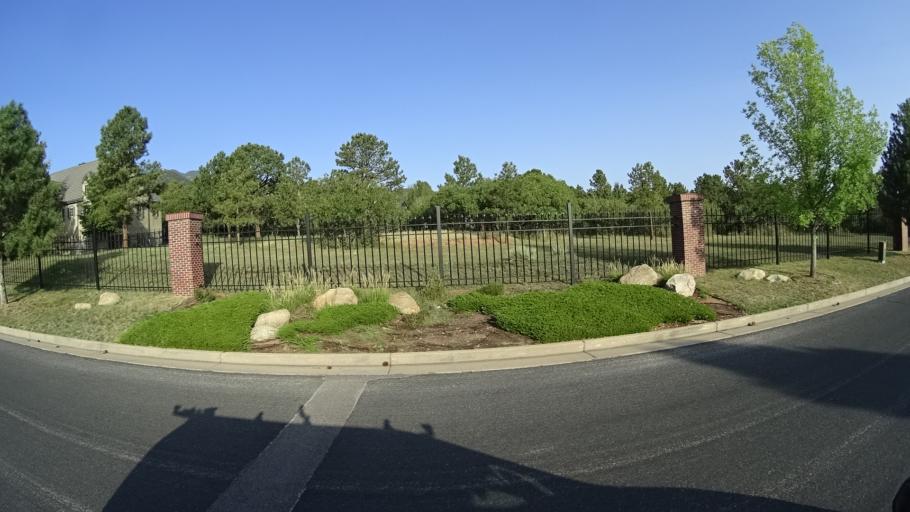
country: US
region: Colorado
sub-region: El Paso County
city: Colorado Springs
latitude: 38.8079
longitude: -104.8610
